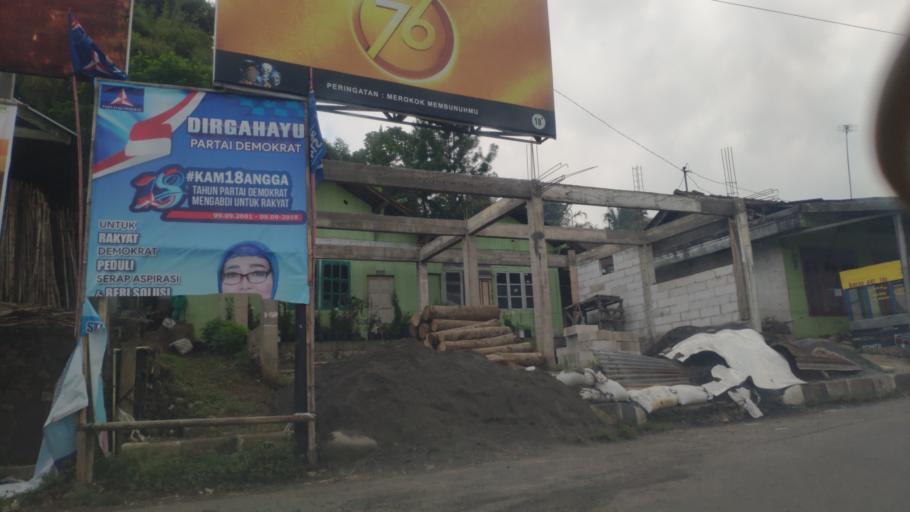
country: ID
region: Central Java
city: Wonosobo
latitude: -7.2468
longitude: 109.7957
